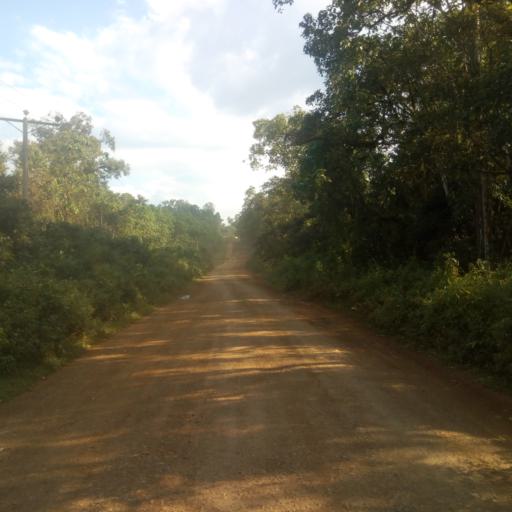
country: ET
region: Oromiya
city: Gore
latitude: 7.8711
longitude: 35.4801
